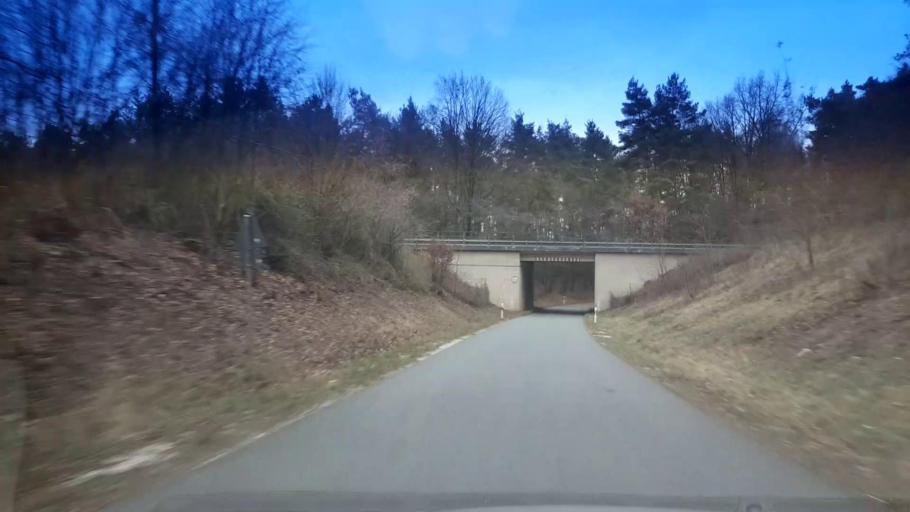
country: DE
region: Bavaria
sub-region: Upper Franconia
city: Pettstadt
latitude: 49.7830
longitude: 10.9154
